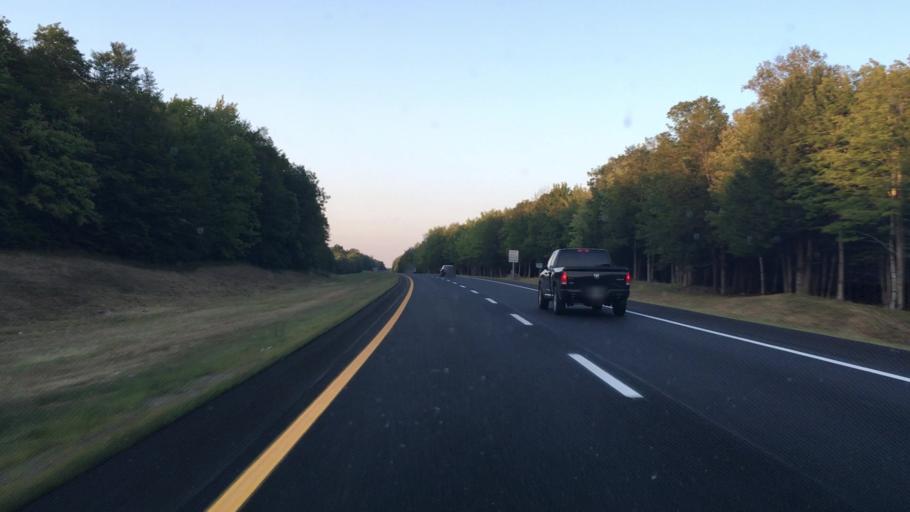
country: US
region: Maine
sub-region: Sagadahoc County
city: Topsham
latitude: 43.9595
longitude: -69.9591
